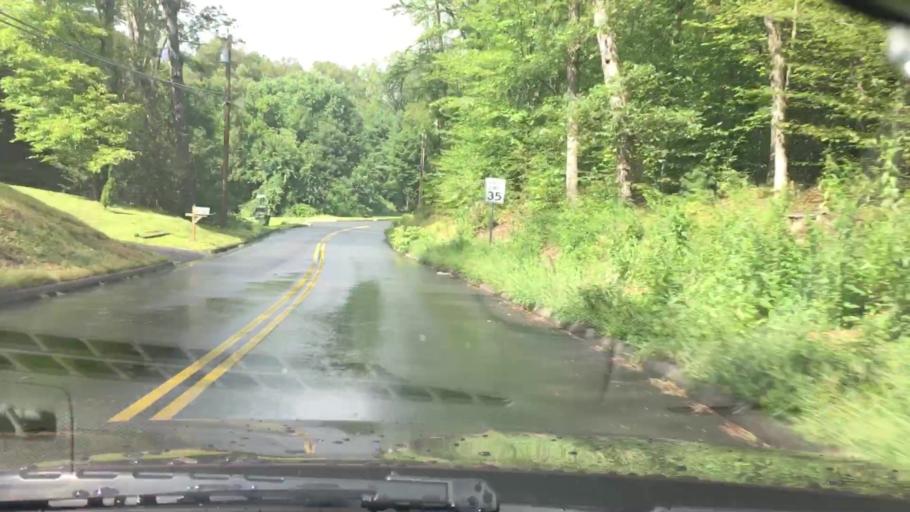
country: US
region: Connecticut
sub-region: Hartford County
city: Manchester
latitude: 41.7246
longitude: -72.5369
